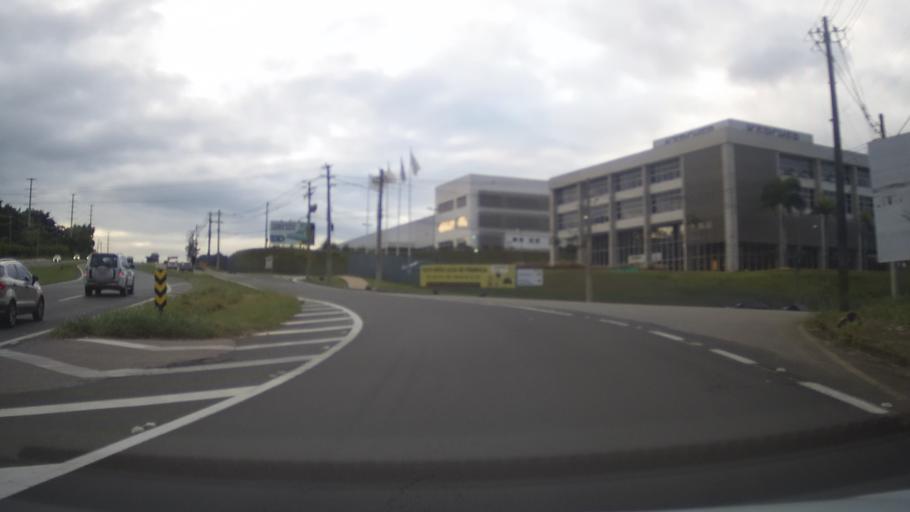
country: BR
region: Sao Paulo
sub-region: Vinhedo
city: Vinhedo
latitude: -23.0616
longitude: -46.9986
